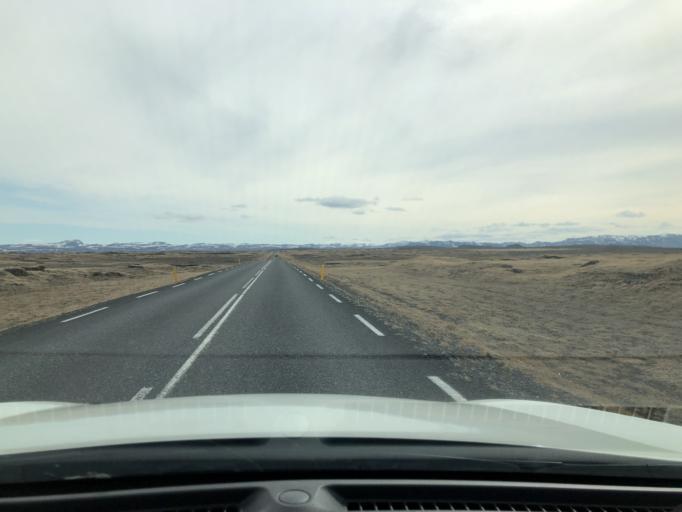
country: IS
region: Northeast
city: Laugar
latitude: 65.6436
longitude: -16.3400
